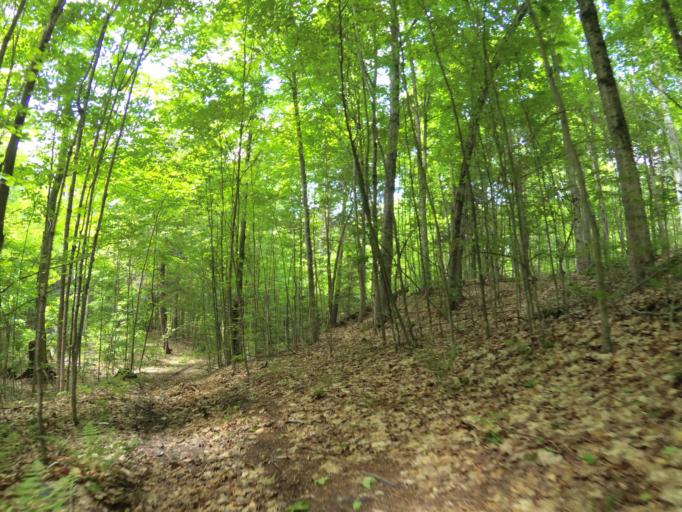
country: CA
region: Ontario
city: Renfrew
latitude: 45.0554
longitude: -76.8462
